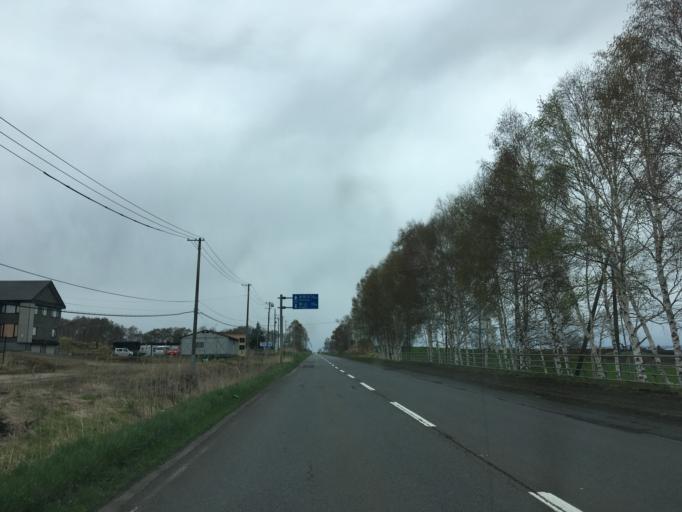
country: JP
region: Hokkaido
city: Chitose
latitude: 42.9164
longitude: 141.8100
